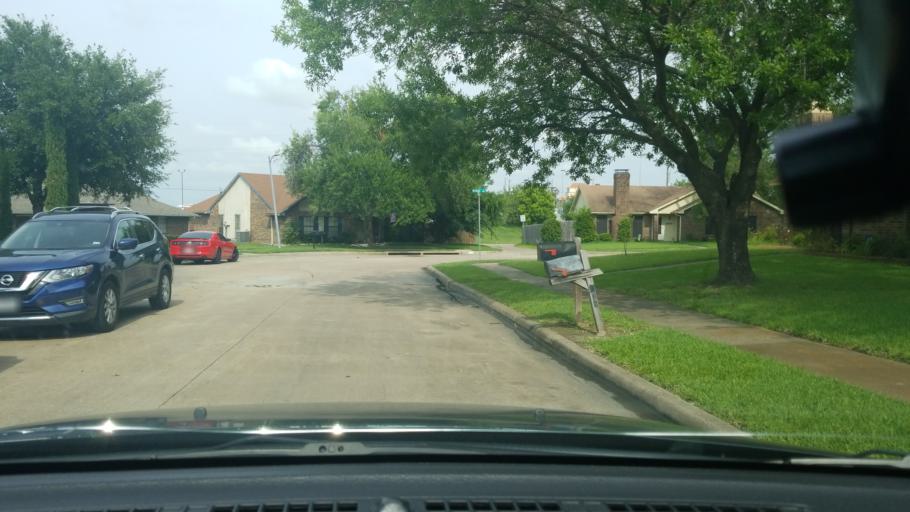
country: US
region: Texas
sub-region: Dallas County
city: Mesquite
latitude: 32.7634
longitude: -96.6283
